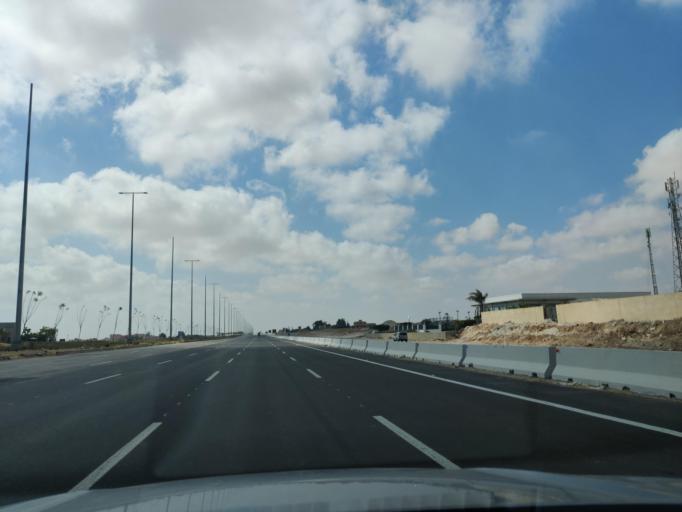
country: EG
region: Muhafazat Matruh
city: Al `Alamayn
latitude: 30.9359
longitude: 28.7871
